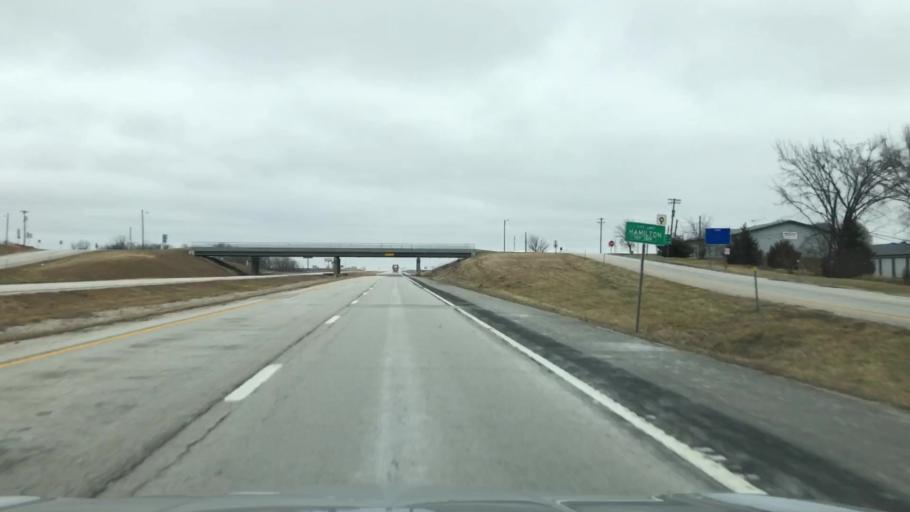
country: US
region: Missouri
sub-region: Caldwell County
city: Hamilton
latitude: 39.7334
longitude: -94.0029
